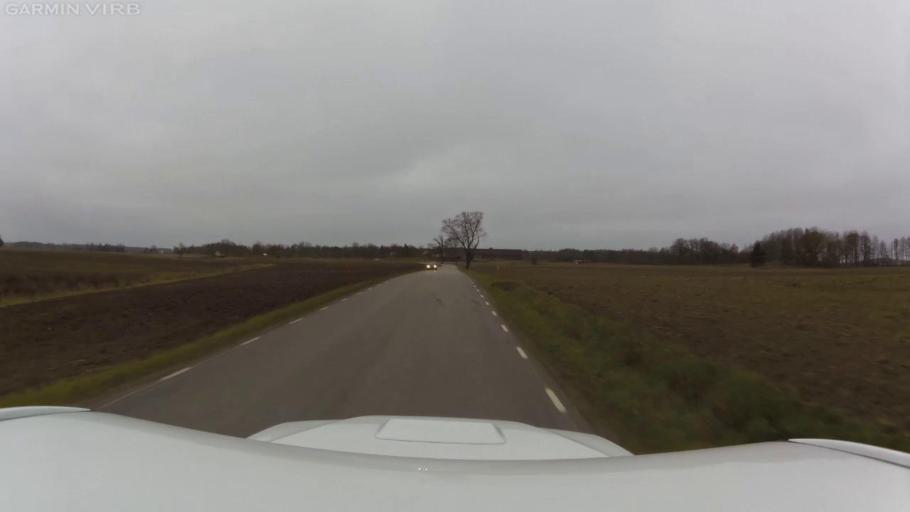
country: SE
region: OEstergoetland
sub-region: Linkopings Kommun
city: Vikingstad
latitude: 58.3701
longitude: 15.4326
